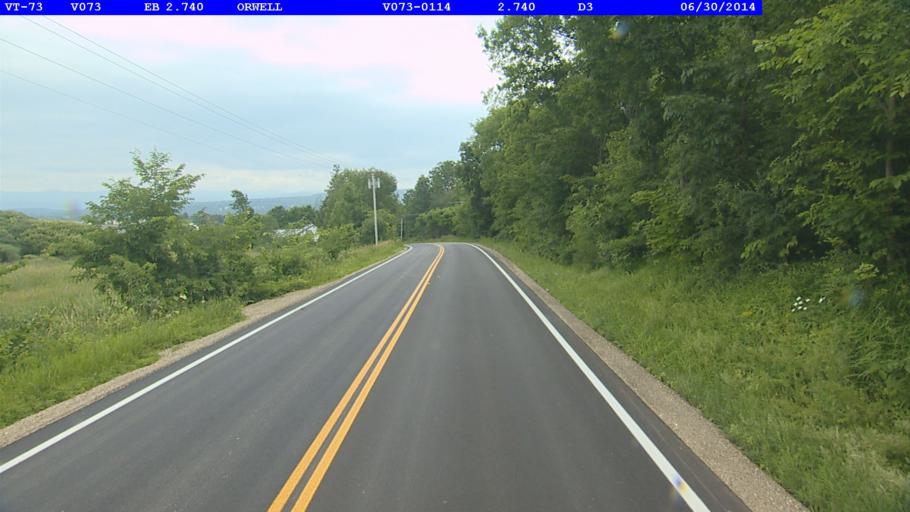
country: US
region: Vermont
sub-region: Rutland County
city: Brandon
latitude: 43.8017
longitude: -73.2523
